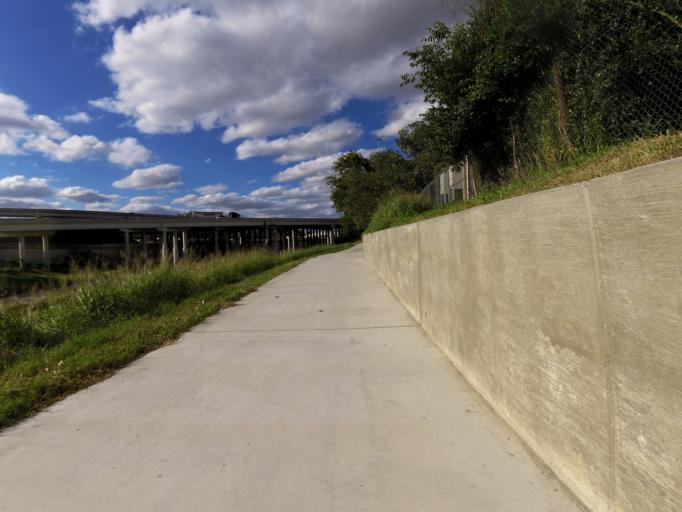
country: US
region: Texas
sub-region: Bexar County
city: San Antonio
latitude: 29.4042
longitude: -98.5096
